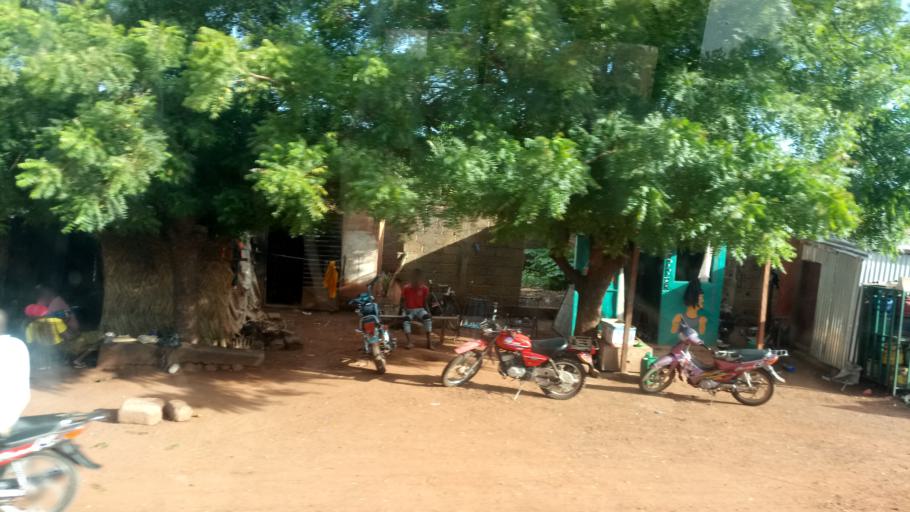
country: ML
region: Sikasso
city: Sikasso
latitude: 11.3122
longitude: -5.6979
